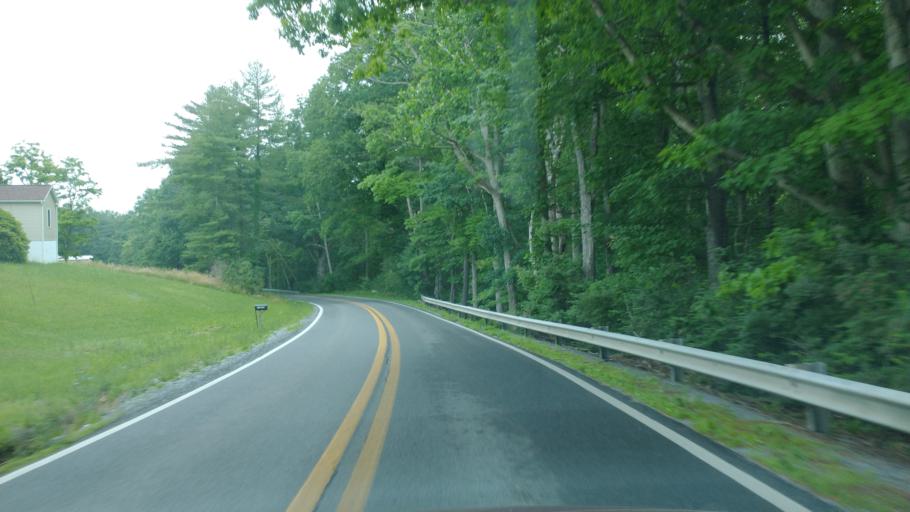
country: US
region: West Virginia
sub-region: Mercer County
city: Athens
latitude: 37.4160
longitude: -81.0449
